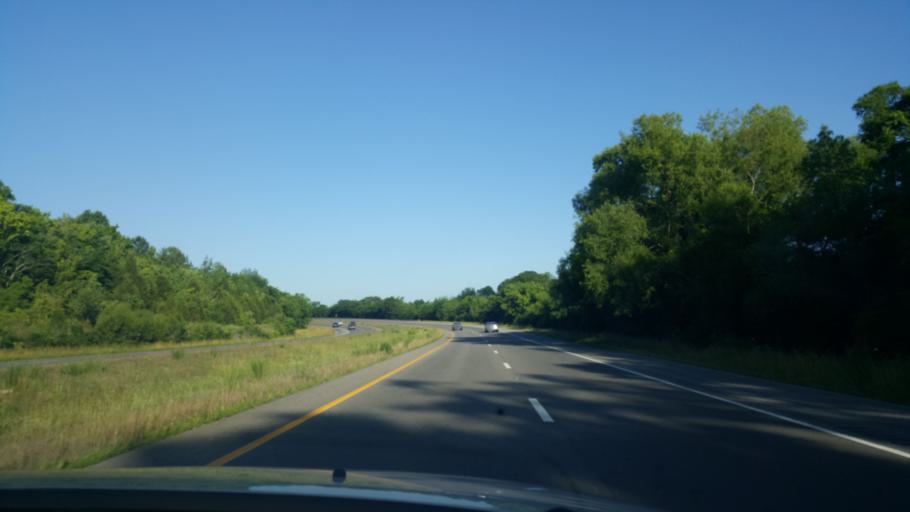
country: US
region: Tennessee
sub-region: Maury County
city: Columbia
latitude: 35.6301
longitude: -87.0977
